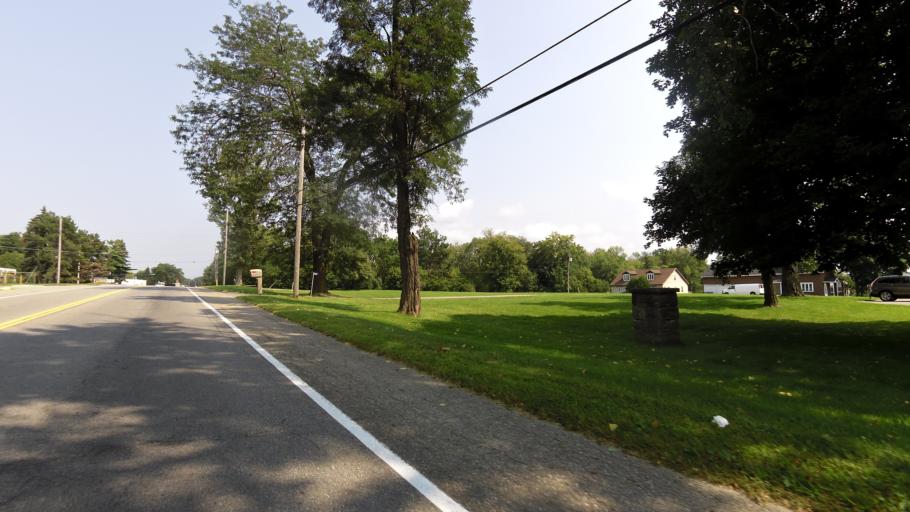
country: CA
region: Ontario
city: Brockville
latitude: 44.6070
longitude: -75.6584
